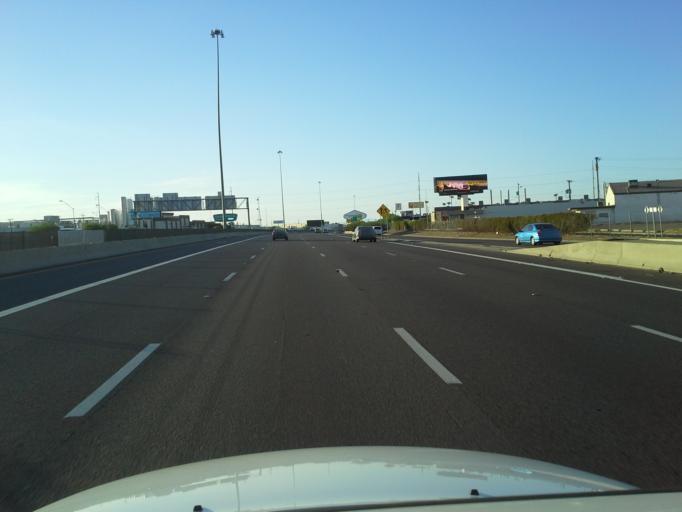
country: US
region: Arizona
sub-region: Maricopa County
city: Phoenix
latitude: 33.4695
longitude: -112.1114
